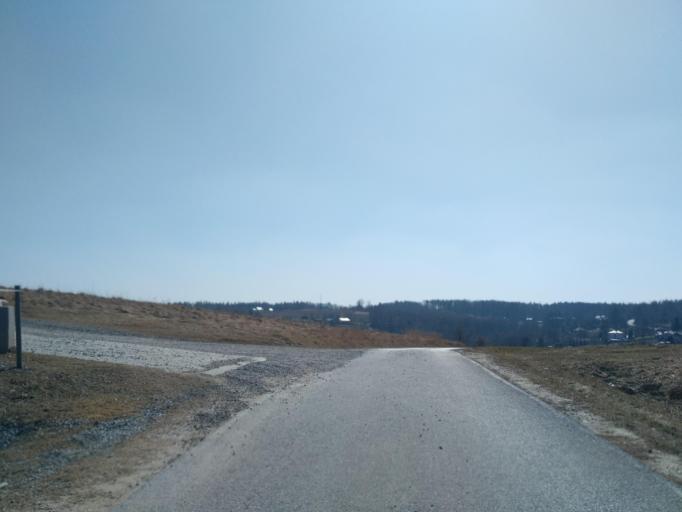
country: PL
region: Subcarpathian Voivodeship
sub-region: Powiat strzyzowski
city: Czudec
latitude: 49.9802
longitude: 21.8391
